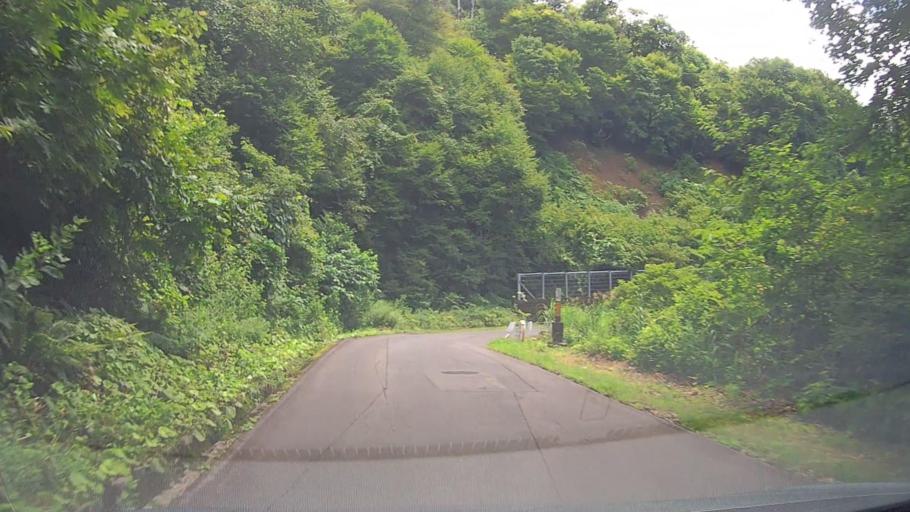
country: JP
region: Nagano
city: Iiyama
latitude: 36.9274
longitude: 138.4699
